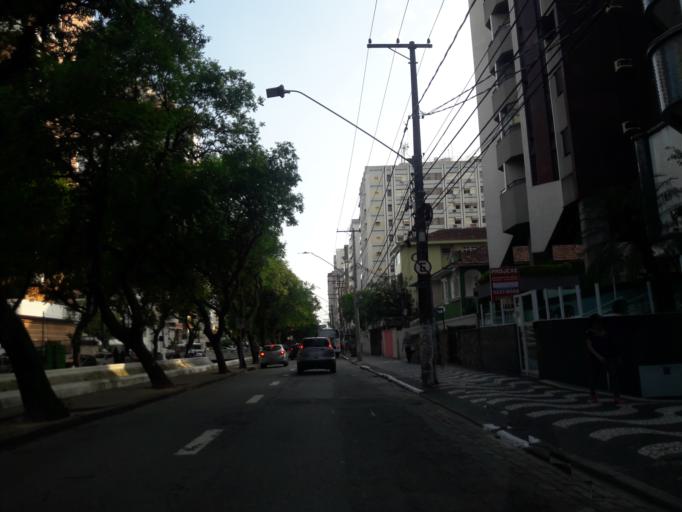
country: BR
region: Sao Paulo
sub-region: Santos
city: Santos
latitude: -23.9646
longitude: -46.3388
